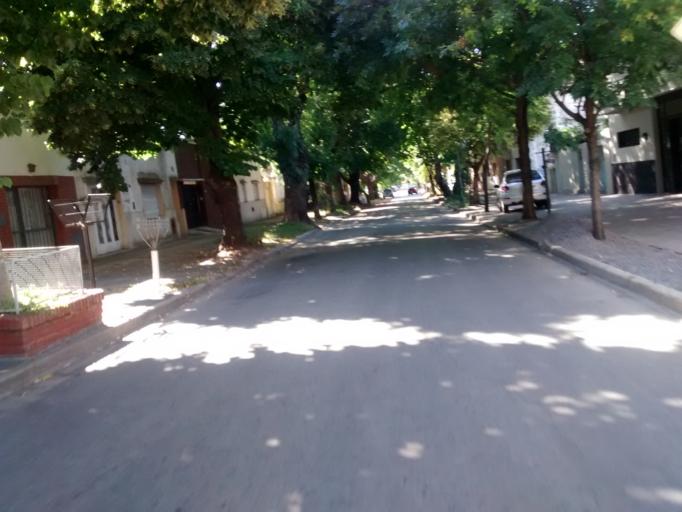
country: AR
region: Buenos Aires
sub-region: Partido de La Plata
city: La Plata
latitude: -34.9193
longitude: -57.9254
